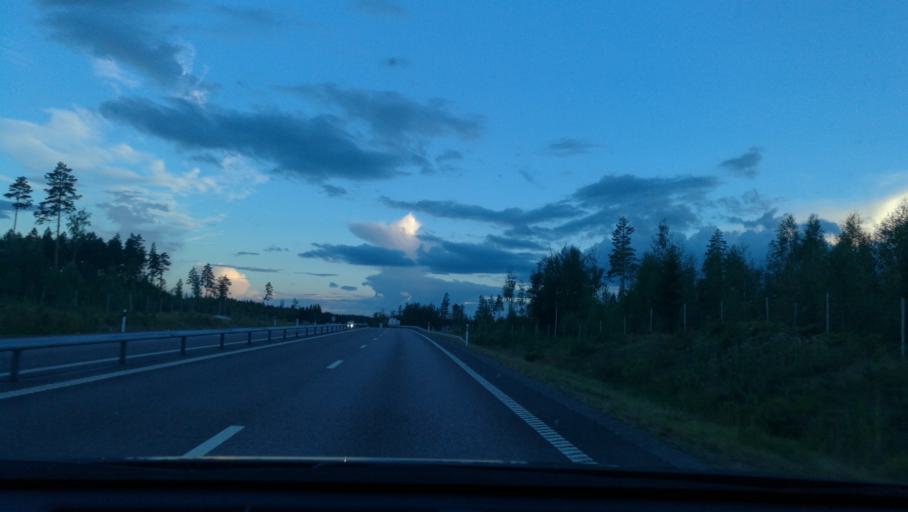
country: SE
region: Soedermanland
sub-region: Katrineholms Kommun
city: Katrineholm
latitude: 58.9529
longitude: 16.2205
